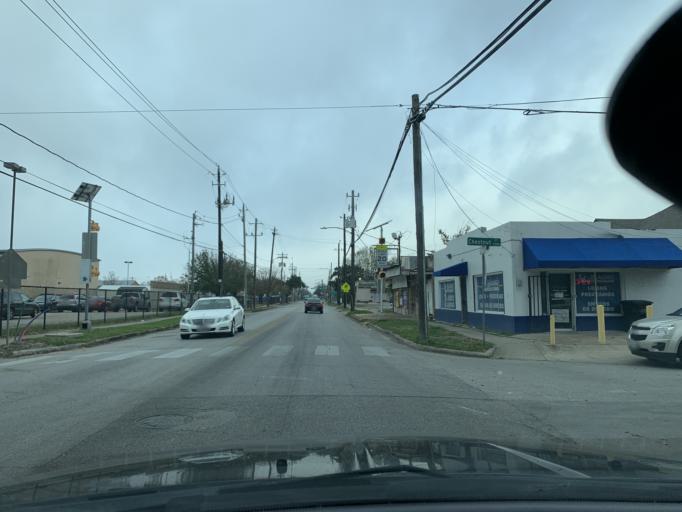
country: US
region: Texas
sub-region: Harris County
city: Houston
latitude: 29.7817
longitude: -95.3614
